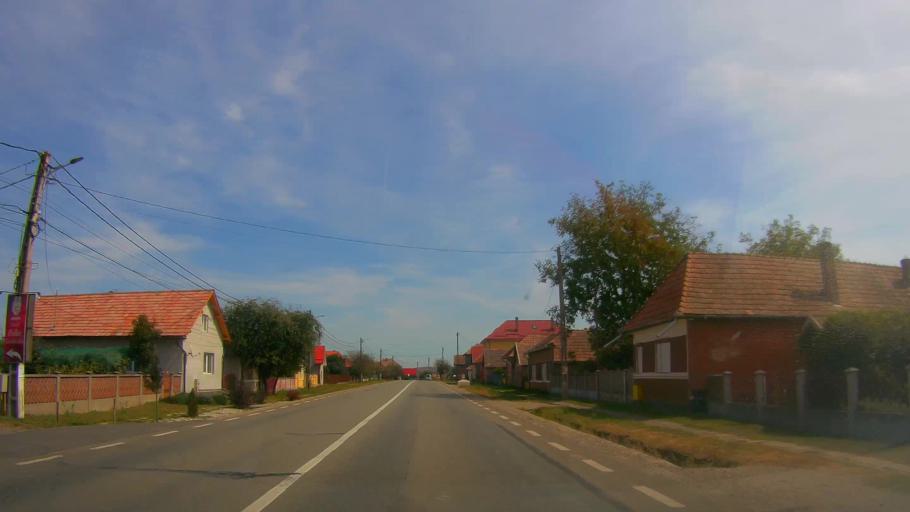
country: RO
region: Mures
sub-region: Comuna Ogra
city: Ogra
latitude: 46.4448
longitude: 24.3232
